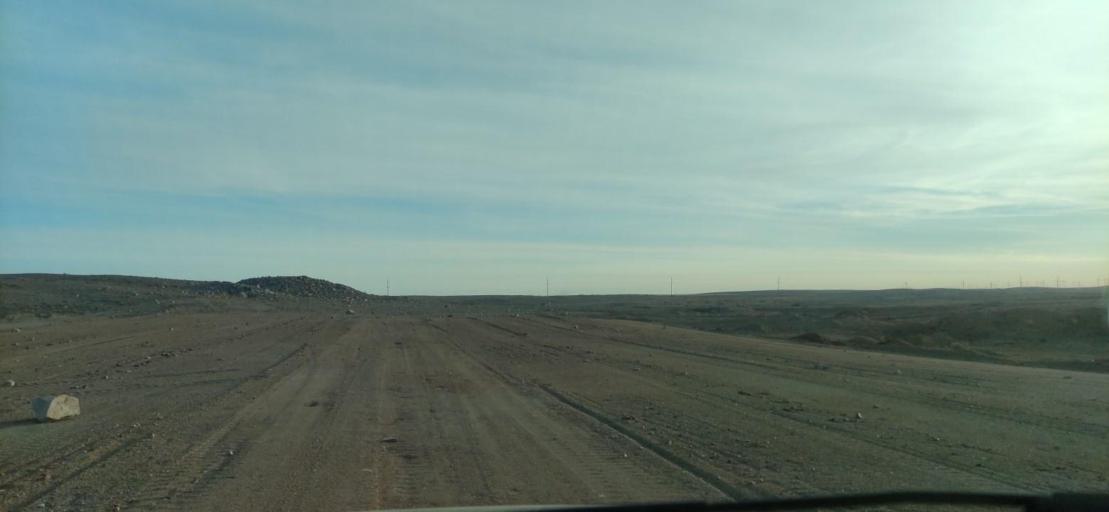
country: KZ
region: Qaraghandy
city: Saryshaghan
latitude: 46.1113
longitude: 73.5957
